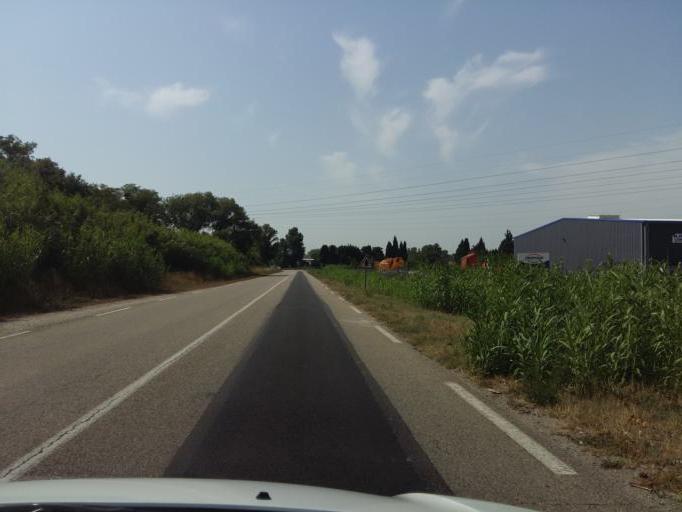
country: FR
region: Provence-Alpes-Cote d'Azur
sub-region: Departement du Vaucluse
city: Bollene
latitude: 44.3157
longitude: 4.7349
